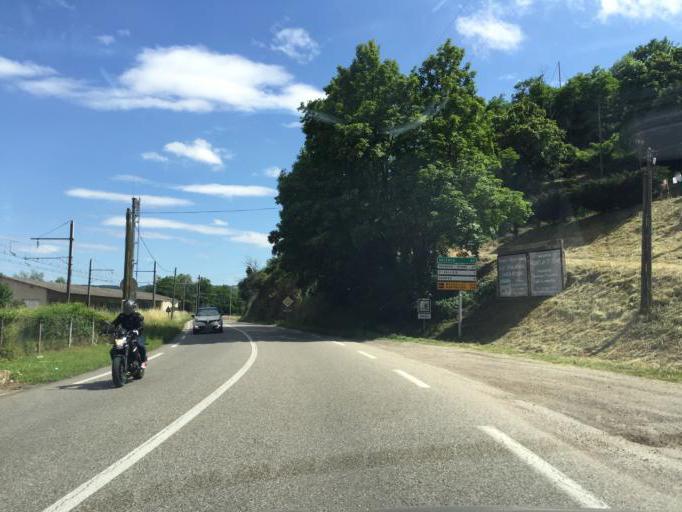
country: FR
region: Rhone-Alpes
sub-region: Departement de l'Ardeche
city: Andance
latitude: 45.2352
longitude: 4.7986
